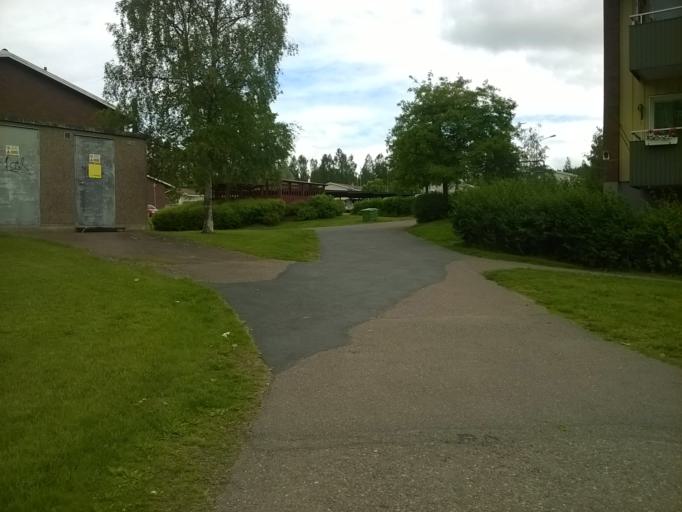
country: SE
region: Dalarna
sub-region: Saters Kommun
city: Saeter
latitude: 60.3413
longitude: 15.7498
